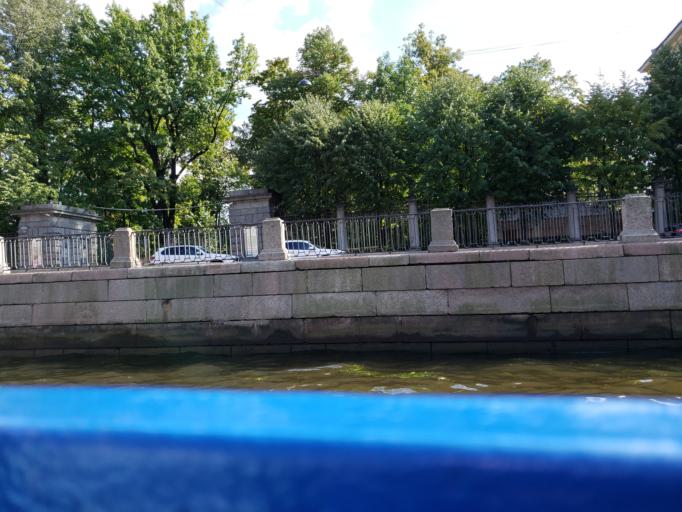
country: RU
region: St.-Petersburg
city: Saint Petersburg
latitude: 59.9201
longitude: 30.3120
